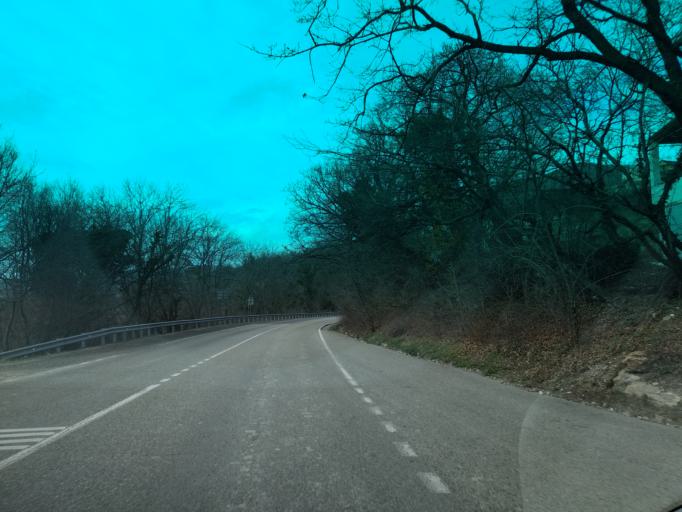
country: RU
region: Krasnodarskiy
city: Tuapse
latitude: 44.0883
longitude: 39.1235
